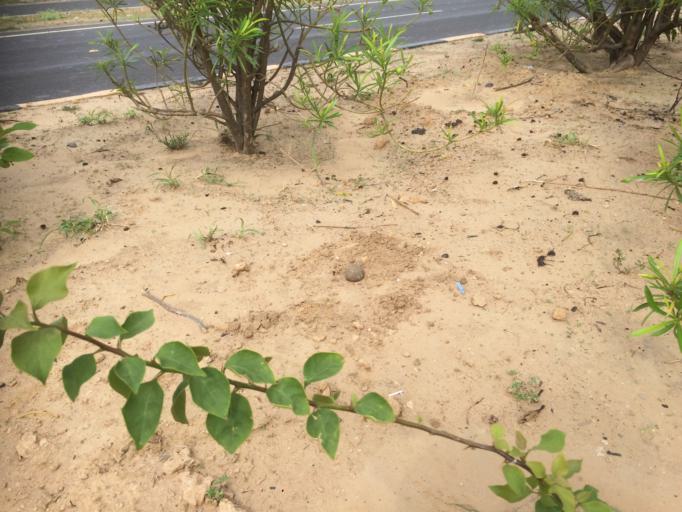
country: IN
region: Gujarat
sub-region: Gandhinagar
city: Adalaj
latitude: 23.1233
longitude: 72.6048
